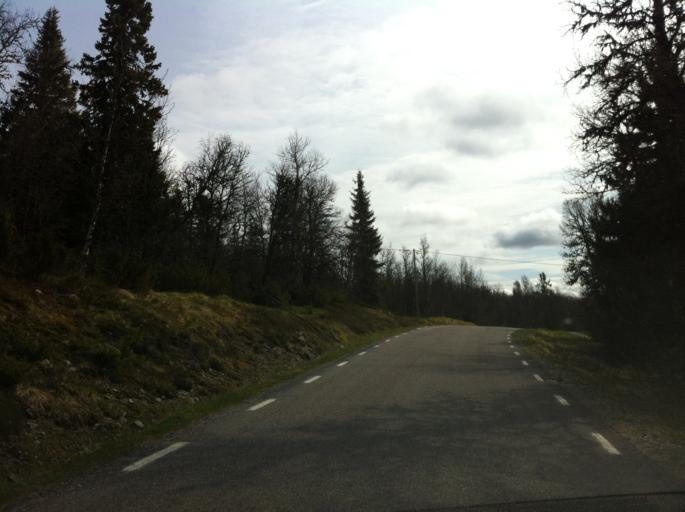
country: NO
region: Hedmark
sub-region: Engerdal
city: Engerdal
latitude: 62.2981
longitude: 12.8043
